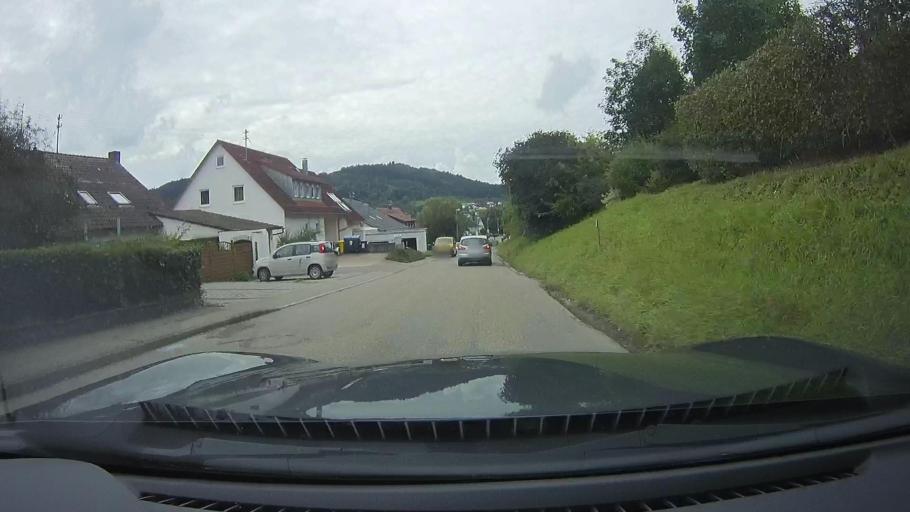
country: DE
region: Baden-Wuerttemberg
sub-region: Regierungsbezirk Stuttgart
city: Murrhardt
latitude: 48.9858
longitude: 9.5801
